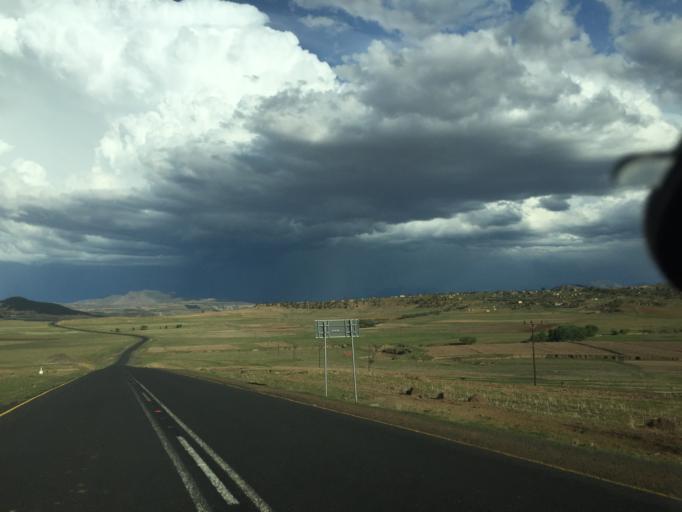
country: LS
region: Berea
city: Teyateyaneng
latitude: -29.0862
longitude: 27.8894
